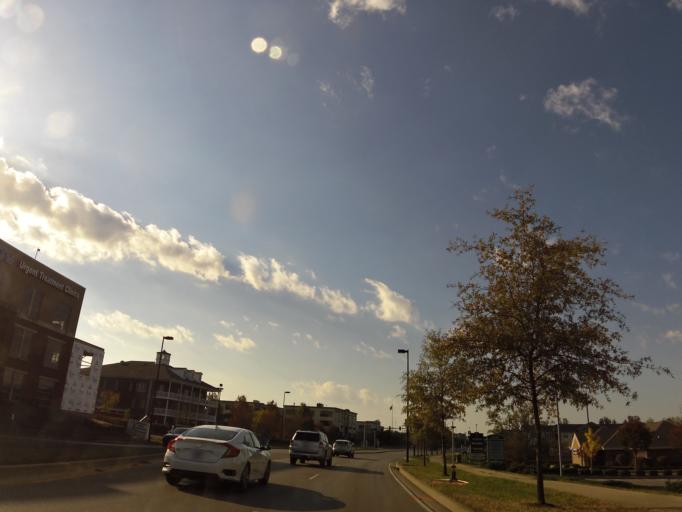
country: US
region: Kentucky
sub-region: Fayette County
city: Lexington-Fayette
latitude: 38.0301
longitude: -84.4206
